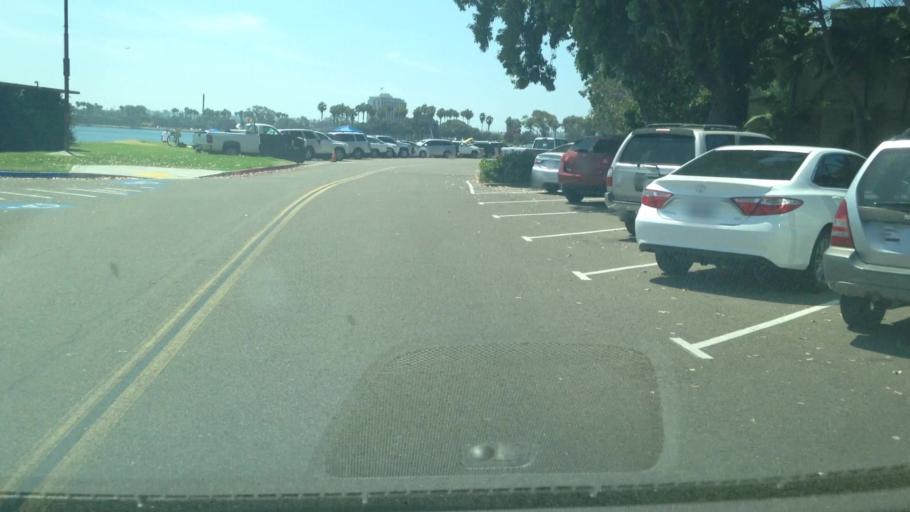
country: US
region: California
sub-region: San Diego County
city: La Jolla
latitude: 32.7746
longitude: -117.2455
